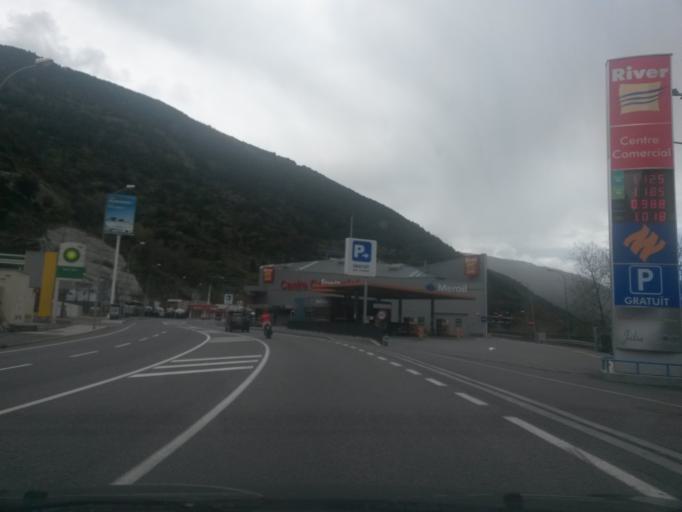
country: AD
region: Sant Julia de Loria
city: Sant Julia de Loria
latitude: 42.4557
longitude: 1.4864
